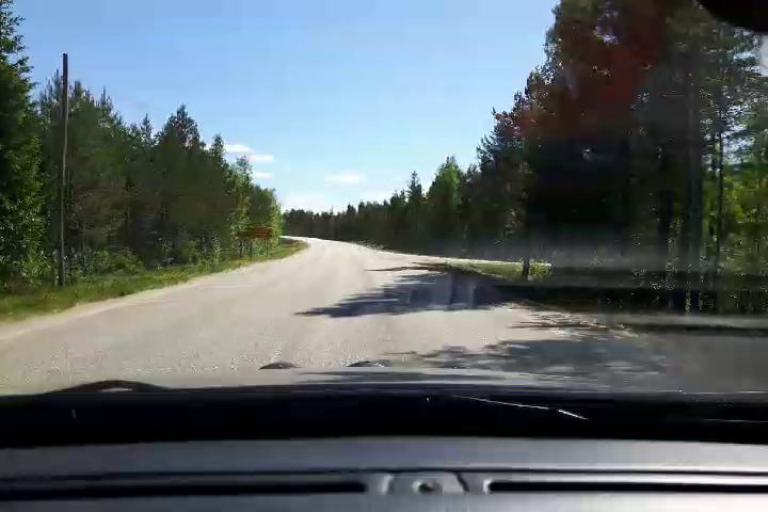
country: SE
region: Jaemtland
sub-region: Harjedalens Kommun
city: Sveg
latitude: 62.1181
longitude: 15.0421
